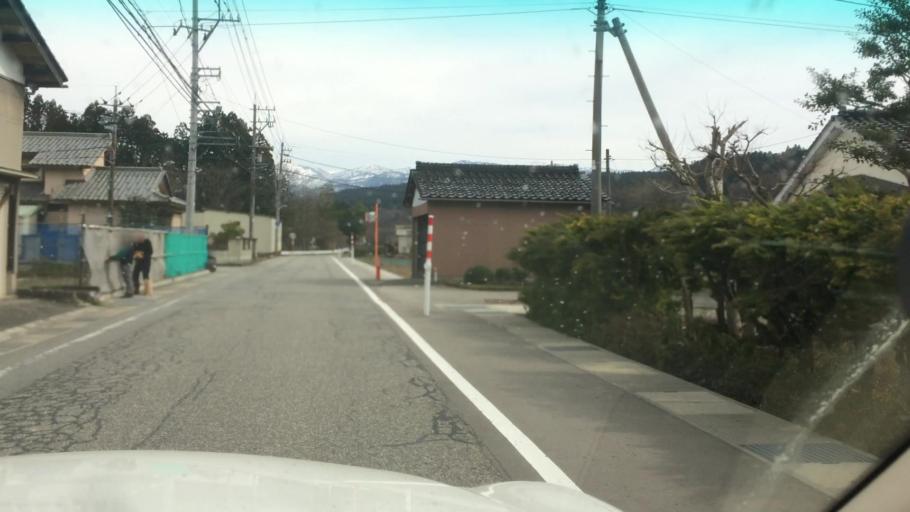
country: JP
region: Toyama
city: Toyama-shi
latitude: 36.6074
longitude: 137.2887
